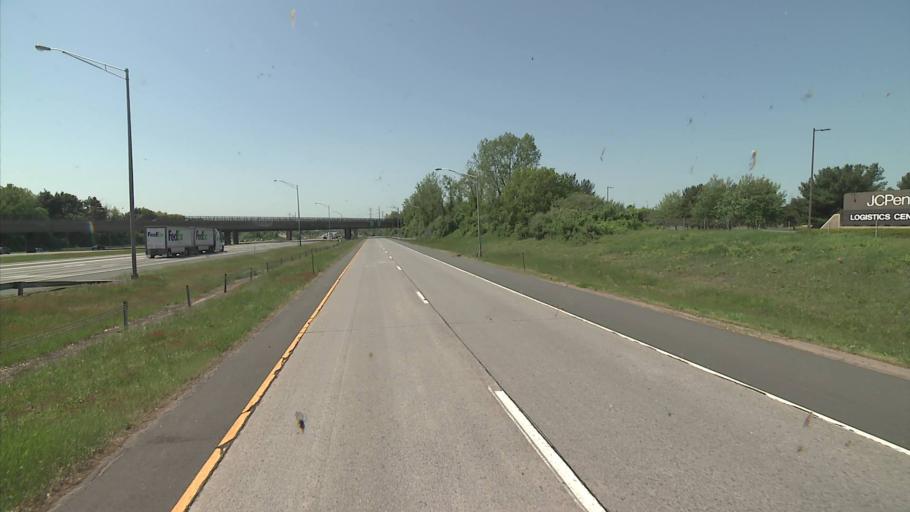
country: US
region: Connecticut
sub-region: Hartford County
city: Manchester
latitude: 41.7977
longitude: -72.5584
